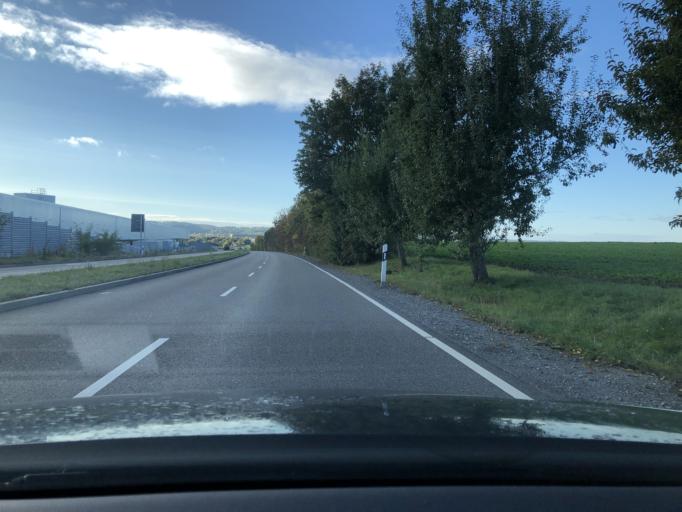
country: DE
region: Baden-Wuerttemberg
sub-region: Regierungsbezirk Stuttgart
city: Magstadt
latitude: 48.7004
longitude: 8.9770
